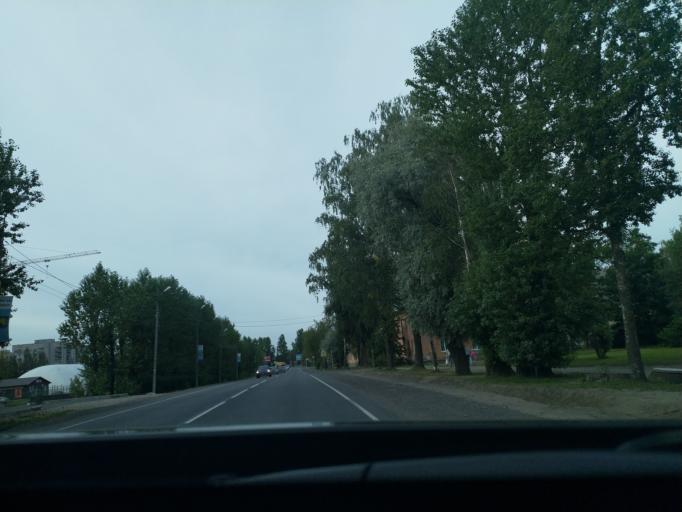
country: RU
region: Leningrad
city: Nikol'skoye
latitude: 59.7053
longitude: 30.7844
